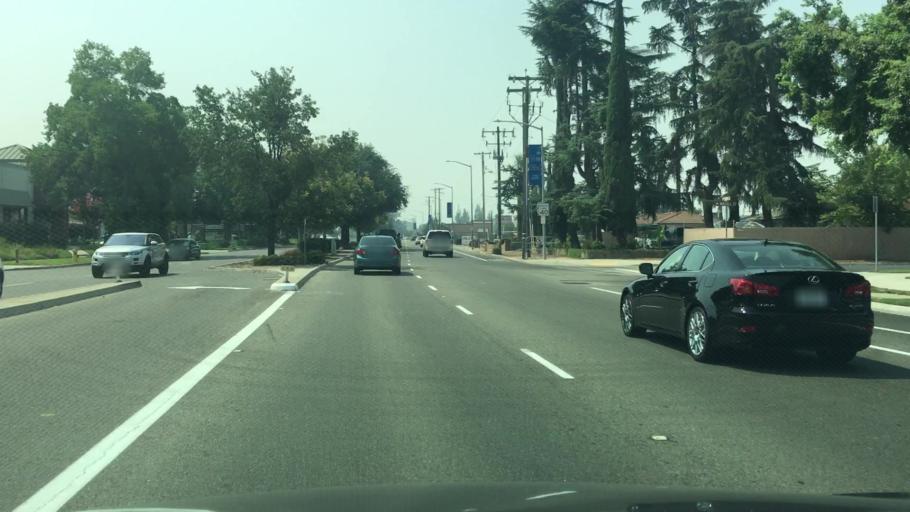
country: US
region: California
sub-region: Fresno County
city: Clovis
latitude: 36.8361
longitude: -119.7001
